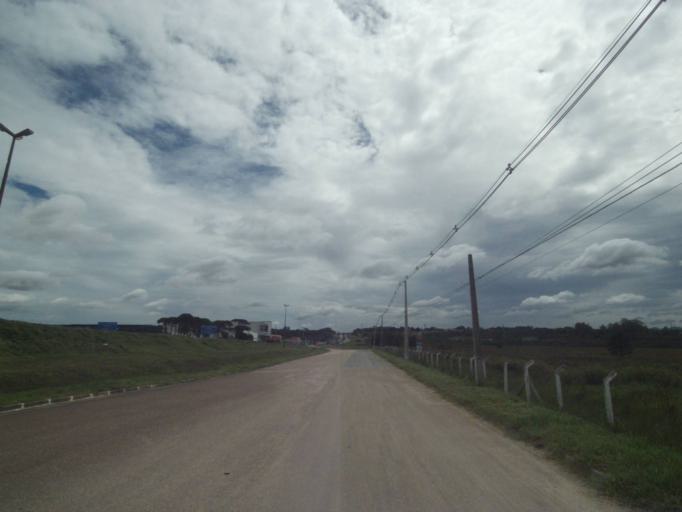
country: BR
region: Parana
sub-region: Sao Jose Dos Pinhais
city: Sao Jose dos Pinhais
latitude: -25.5312
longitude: -49.1436
